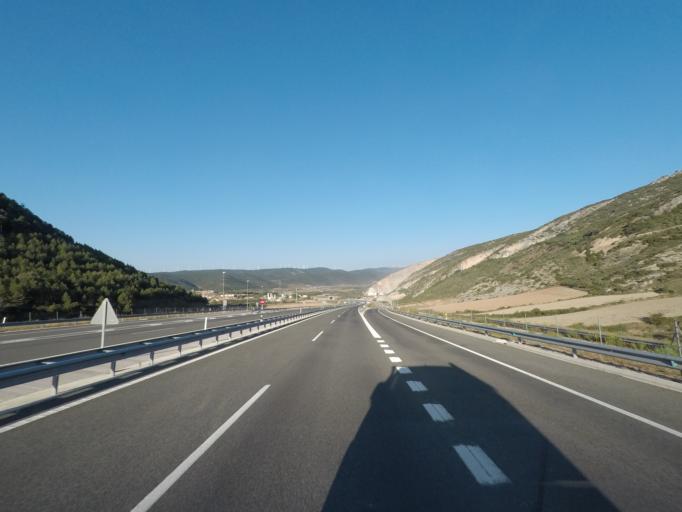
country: ES
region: Navarre
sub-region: Provincia de Navarra
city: Liedena
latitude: 42.6240
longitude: -1.2653
